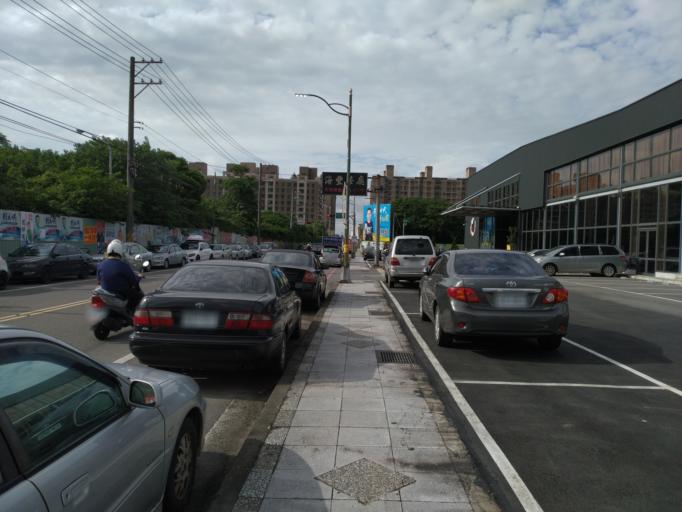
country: TW
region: Taiwan
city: Taoyuan City
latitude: 24.9753
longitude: 121.2532
